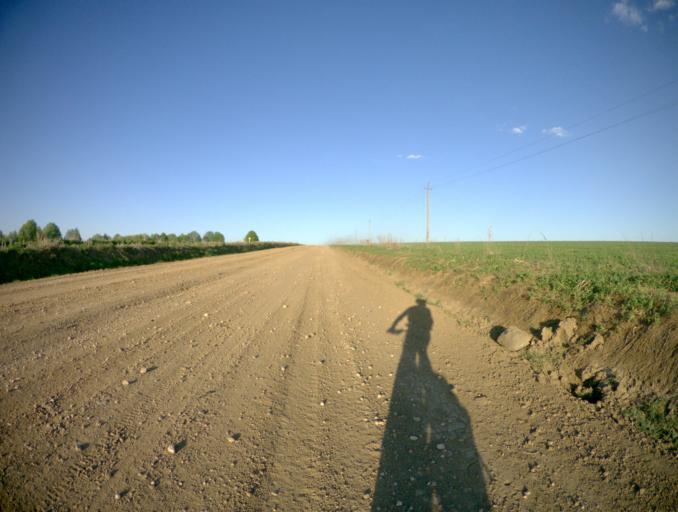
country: RU
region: Ivanovo
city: Gavrilov Posad
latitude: 56.4252
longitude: 40.1067
